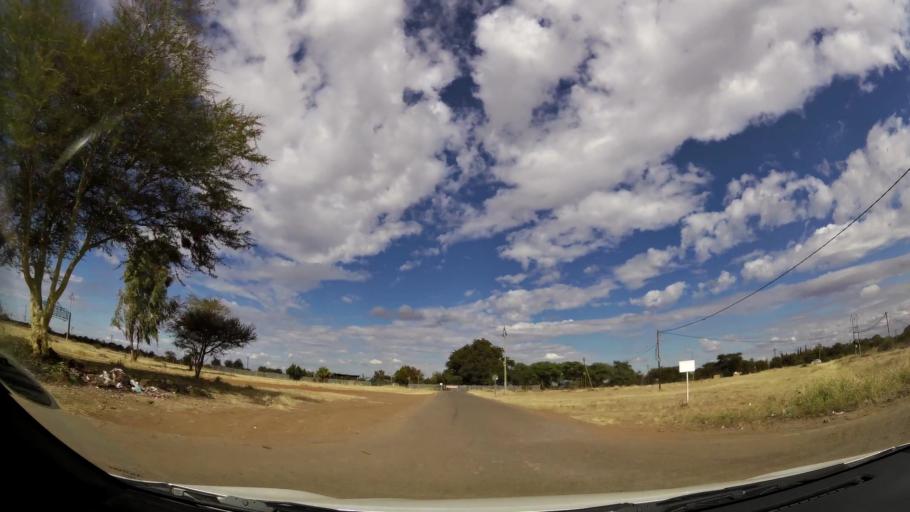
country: ZA
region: Limpopo
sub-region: Waterberg District Municipality
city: Bela-Bela
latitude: -24.8906
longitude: 28.3056
